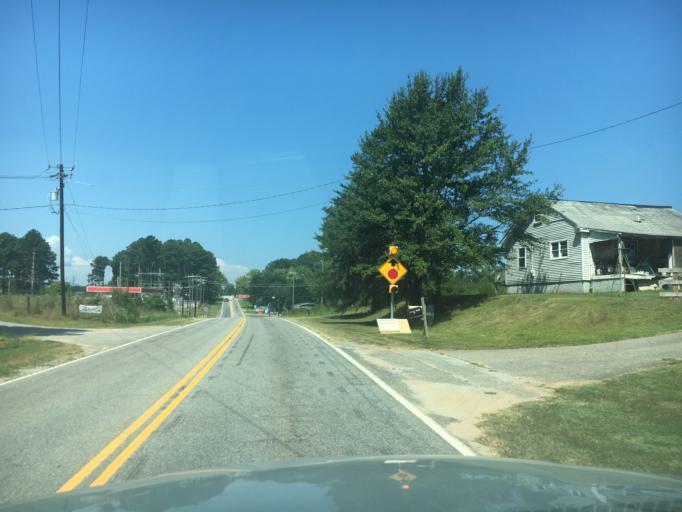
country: US
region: South Carolina
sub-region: Spartanburg County
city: Inman
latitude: 35.1313
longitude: -82.0425
